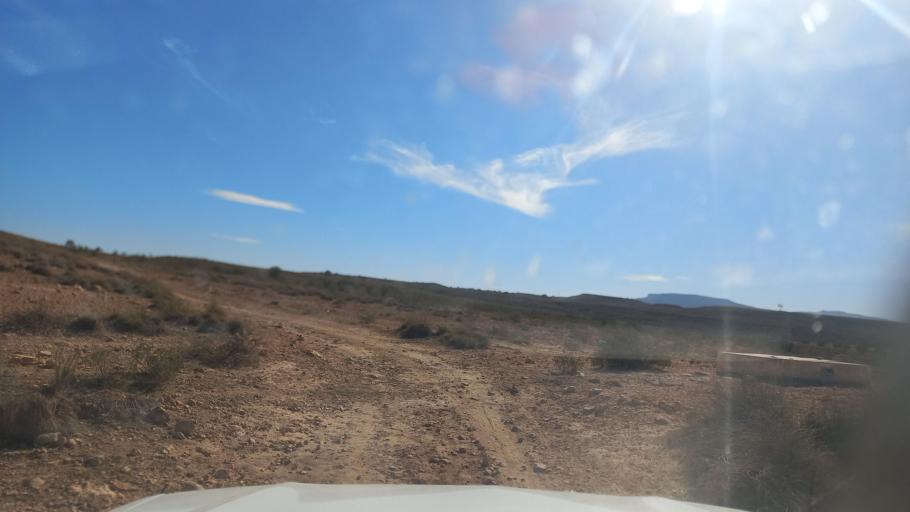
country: TN
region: Al Qasrayn
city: Kasserine
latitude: 35.2053
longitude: 8.9770
